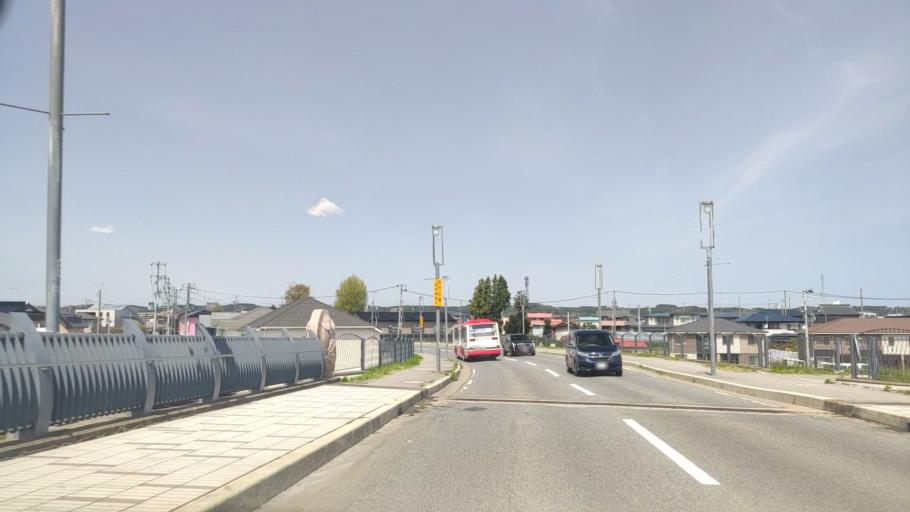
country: JP
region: Aomori
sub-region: Hachinohe Shi
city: Uchimaru
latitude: 40.5021
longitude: 141.4424
